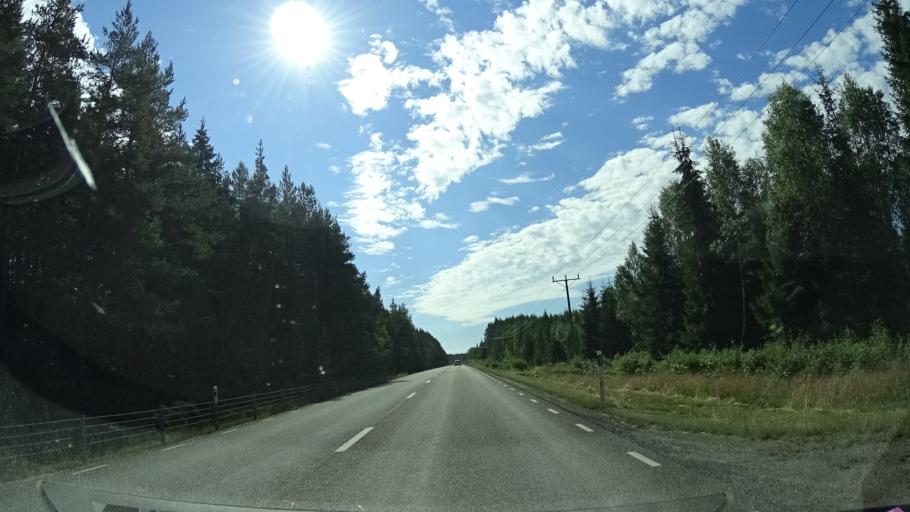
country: SE
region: Vaermland
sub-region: Arjangs Kommun
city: Arjaeng
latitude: 59.4571
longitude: 12.0358
